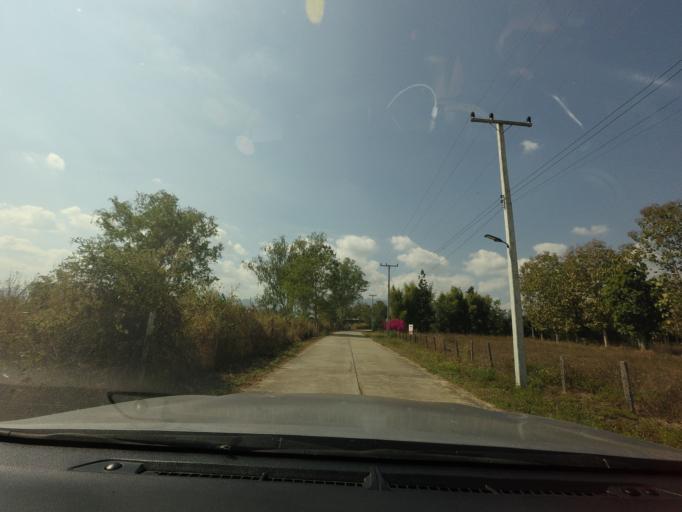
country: TH
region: Mae Hong Son
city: Wiang Nuea
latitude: 19.3828
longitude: 98.4289
